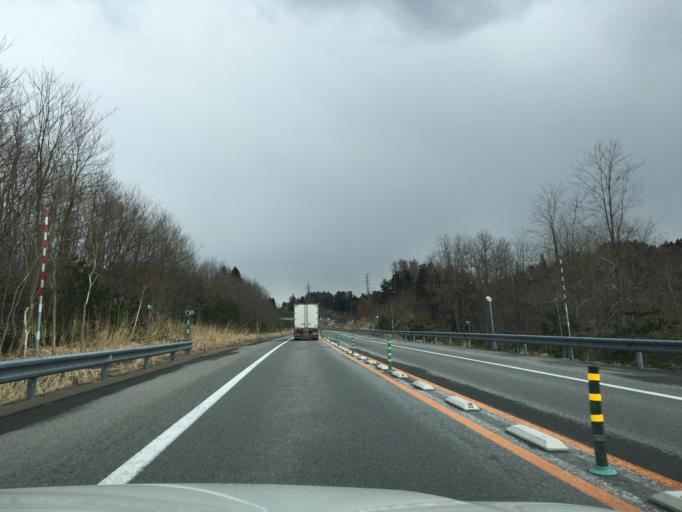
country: JP
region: Aomori
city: Aomori Shi
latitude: 40.8016
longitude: 140.6971
